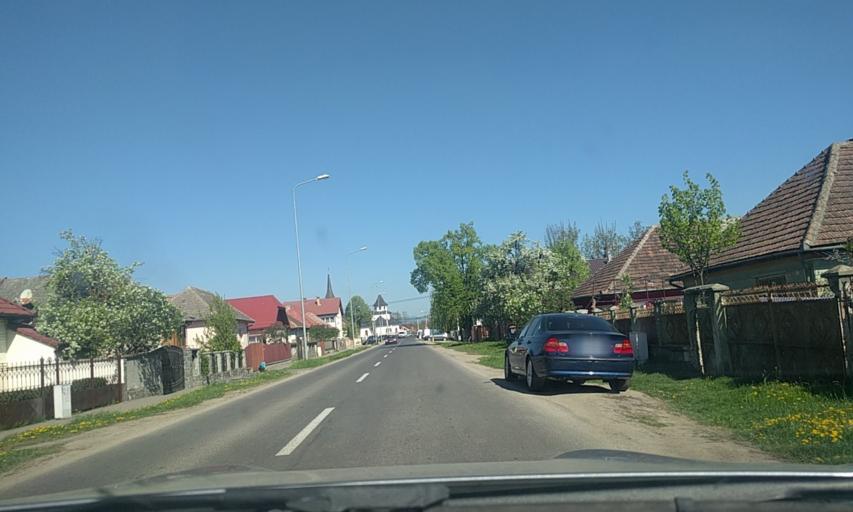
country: RO
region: Brasov
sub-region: Comuna Ghimbav
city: Ghimbav
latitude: 45.6967
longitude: 25.5596
